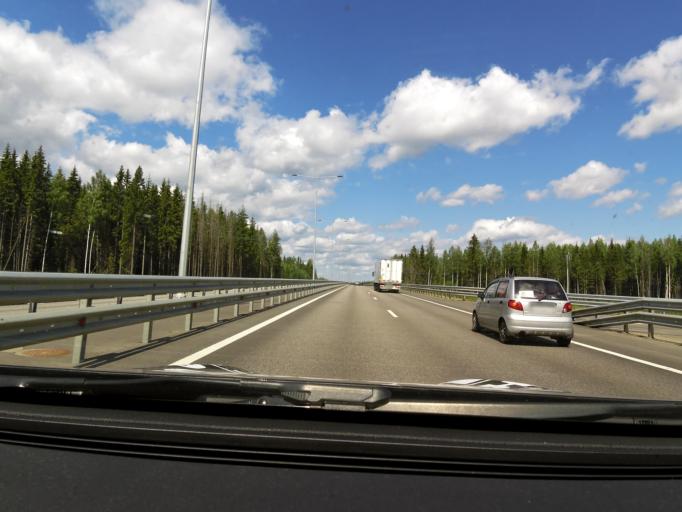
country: RU
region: Tverskaya
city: Vyshniy Volochek
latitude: 57.3962
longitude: 34.5423
